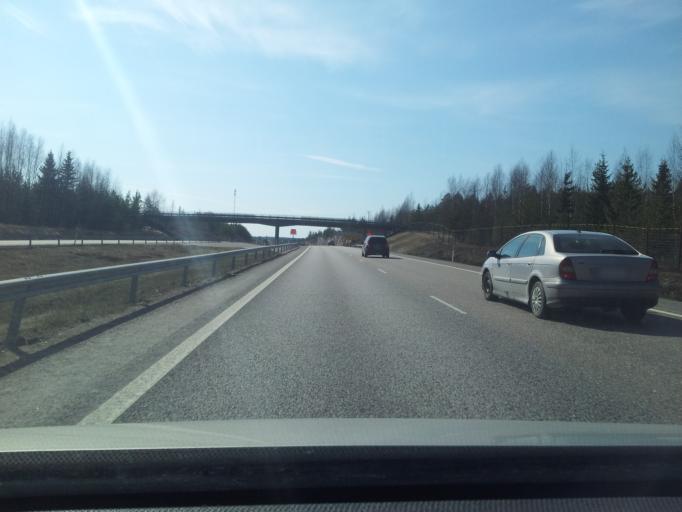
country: FI
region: Kymenlaakso
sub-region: Kotka-Hamina
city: Karhula
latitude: 60.5636
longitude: 27.0267
